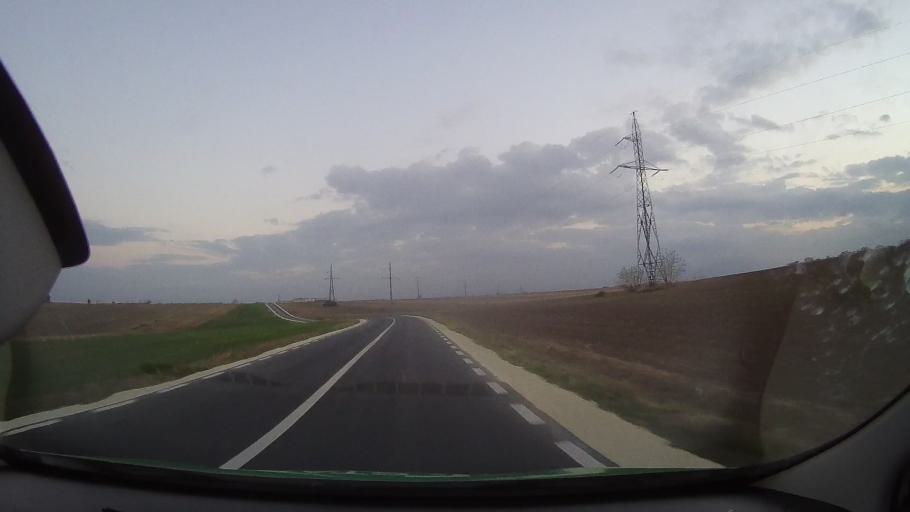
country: RO
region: Constanta
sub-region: Comuna Baneasa
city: Baneasa
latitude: 44.1065
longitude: 27.6712
